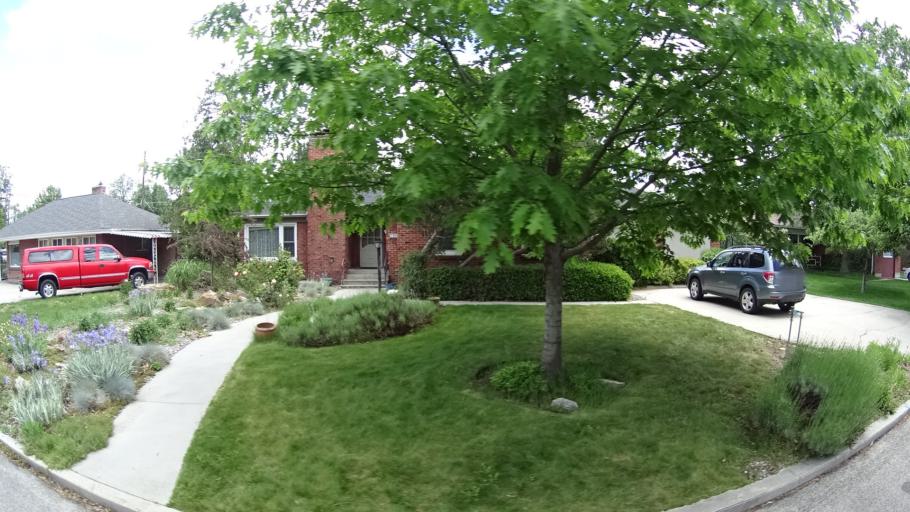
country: US
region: Idaho
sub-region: Ada County
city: Boise
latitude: 43.5894
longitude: -116.1986
